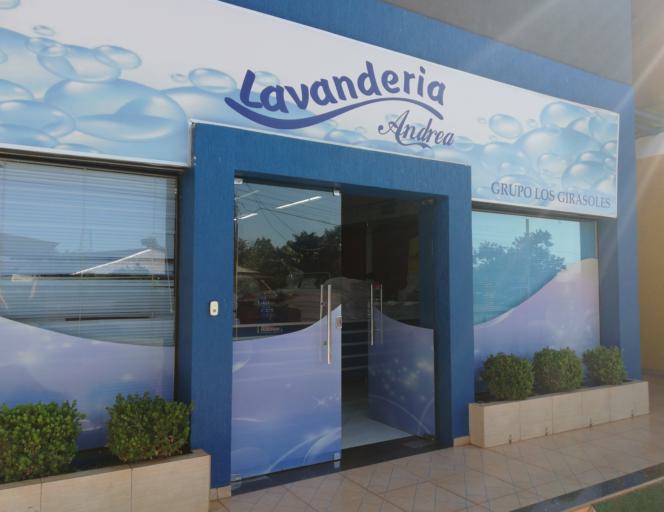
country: PY
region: Alto Parana
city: Ciudad del Este
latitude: -25.5031
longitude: -54.6436
